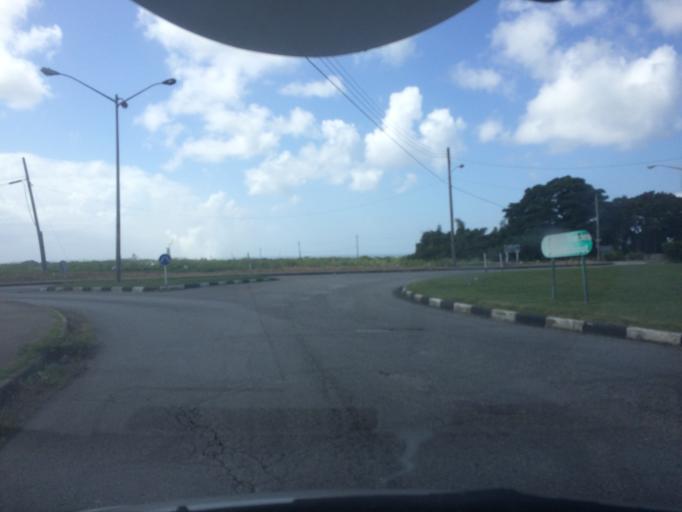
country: BB
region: Saint Lucy
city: Checker Hall
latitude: 13.2913
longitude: -59.6233
